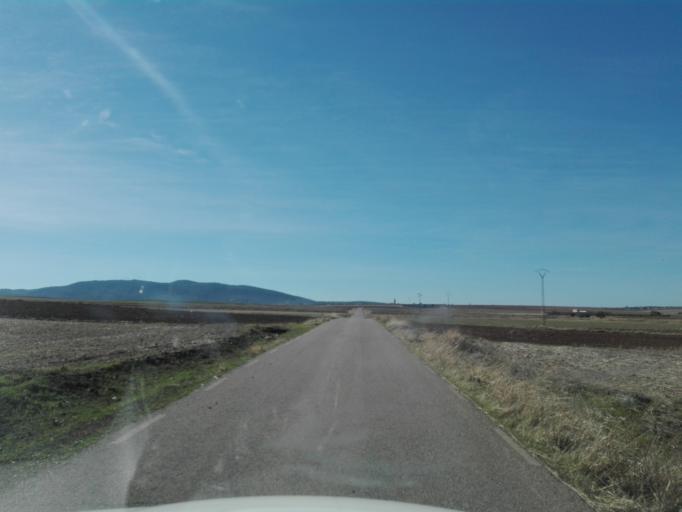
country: ES
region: Extremadura
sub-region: Provincia de Badajoz
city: Llerena
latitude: 38.2634
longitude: -5.9874
